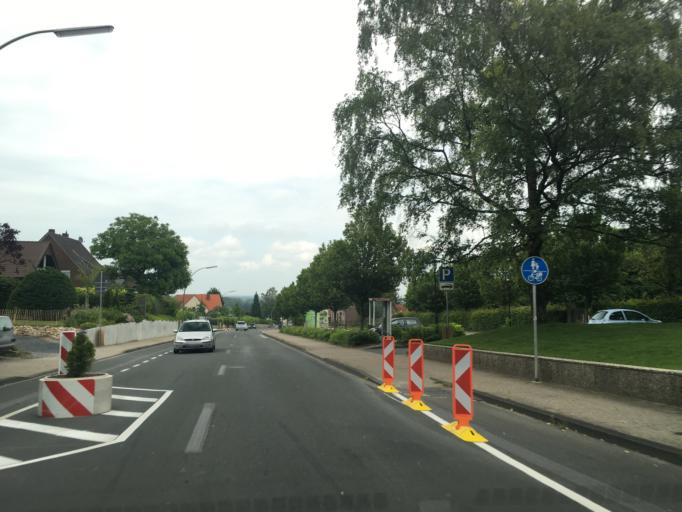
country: DE
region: North Rhine-Westphalia
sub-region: Regierungsbezirk Munster
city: Altenberge
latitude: 52.0475
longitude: 7.4716
